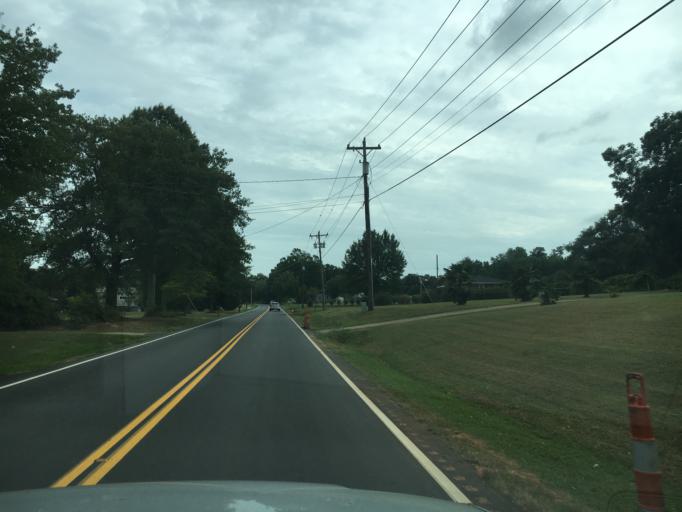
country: US
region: South Carolina
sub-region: Spartanburg County
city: Duncan
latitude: 34.8961
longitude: -82.1435
